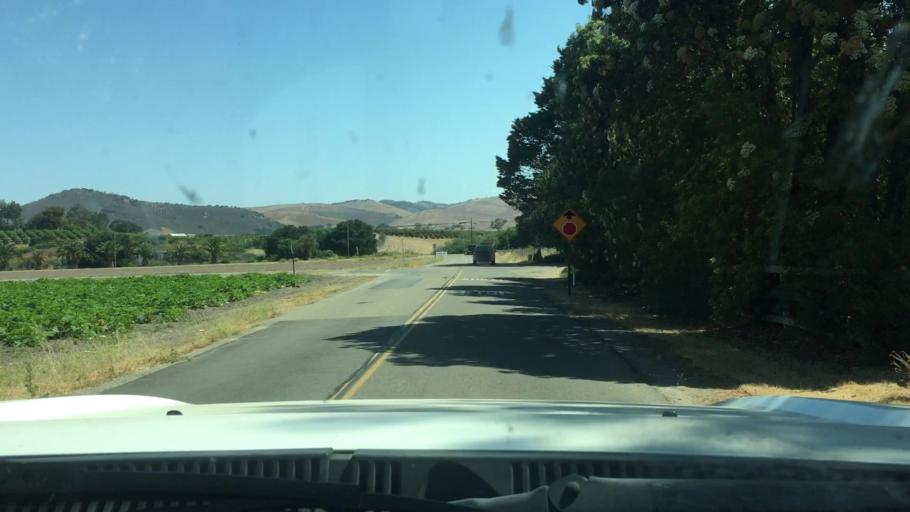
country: US
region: California
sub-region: San Luis Obispo County
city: Callender
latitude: 35.0784
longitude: -120.5485
